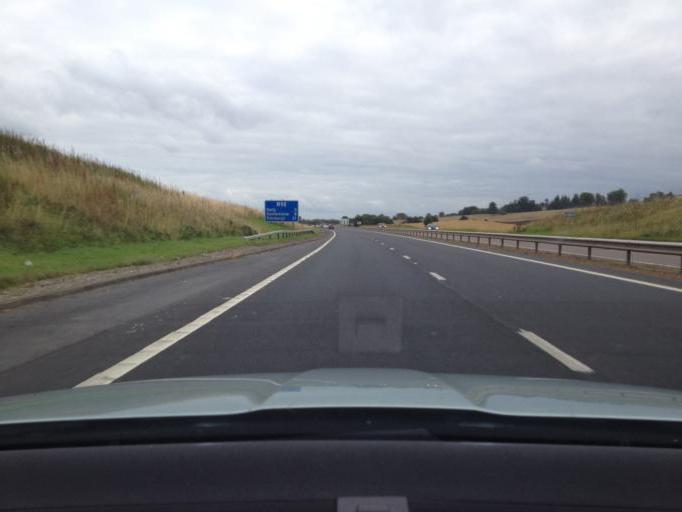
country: GB
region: Scotland
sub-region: Fife
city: Kelty
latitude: 56.1580
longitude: -3.4005
